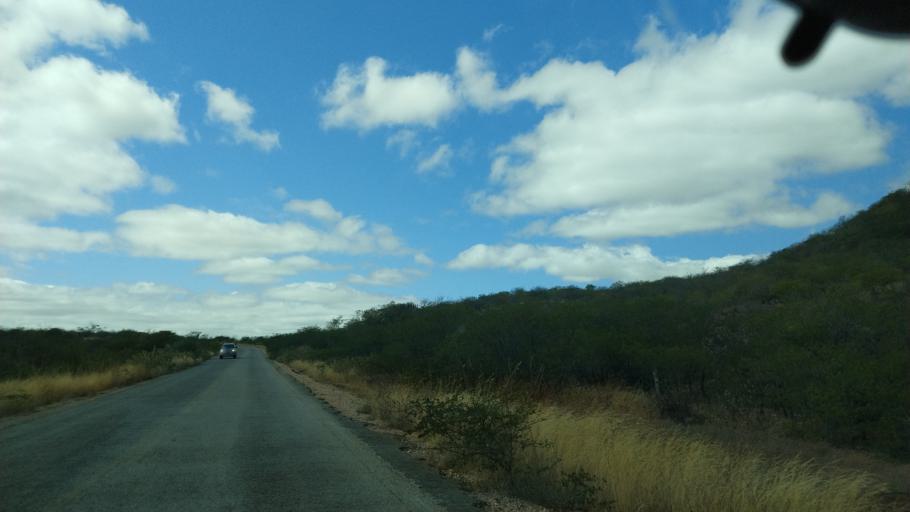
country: BR
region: Rio Grande do Norte
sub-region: Currais Novos
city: Currais Novos
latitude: -6.2687
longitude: -36.5592
